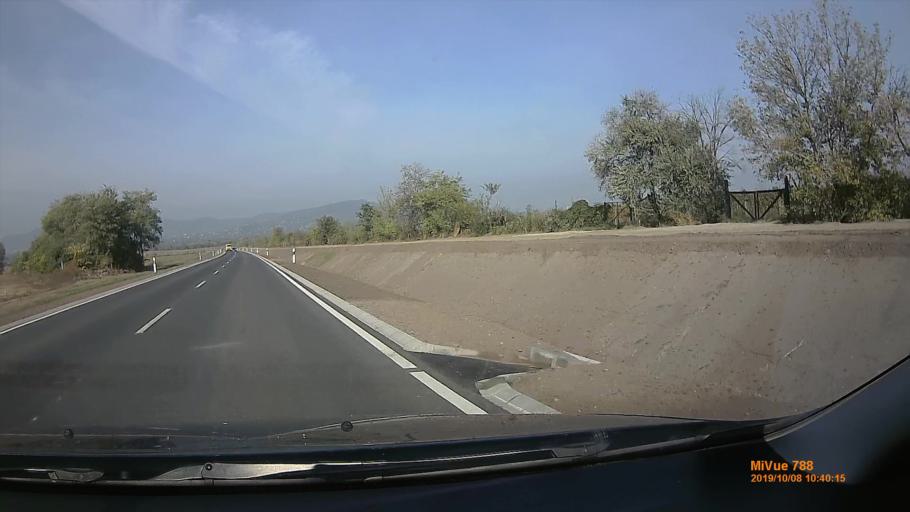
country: HU
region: Pest
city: Dunakeszi
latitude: 47.6606
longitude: 19.1481
